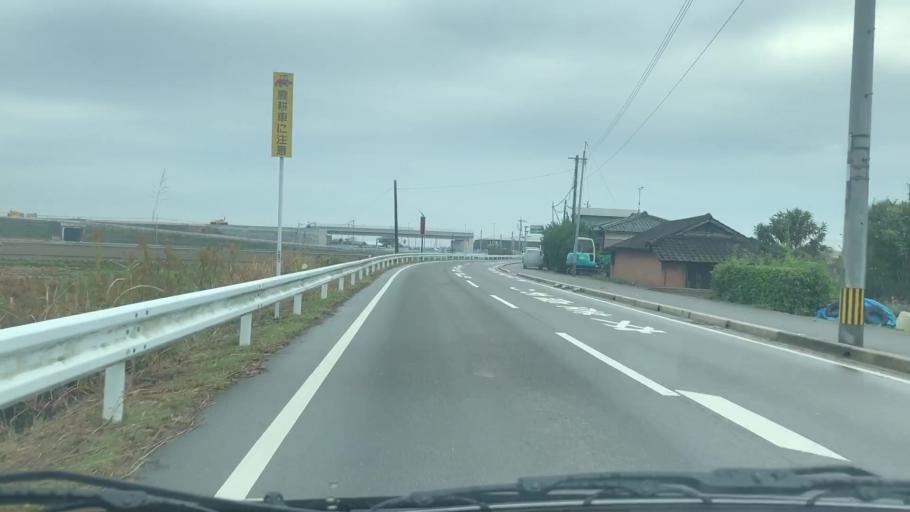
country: JP
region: Saga Prefecture
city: Saga-shi
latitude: 33.2039
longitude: 130.2118
